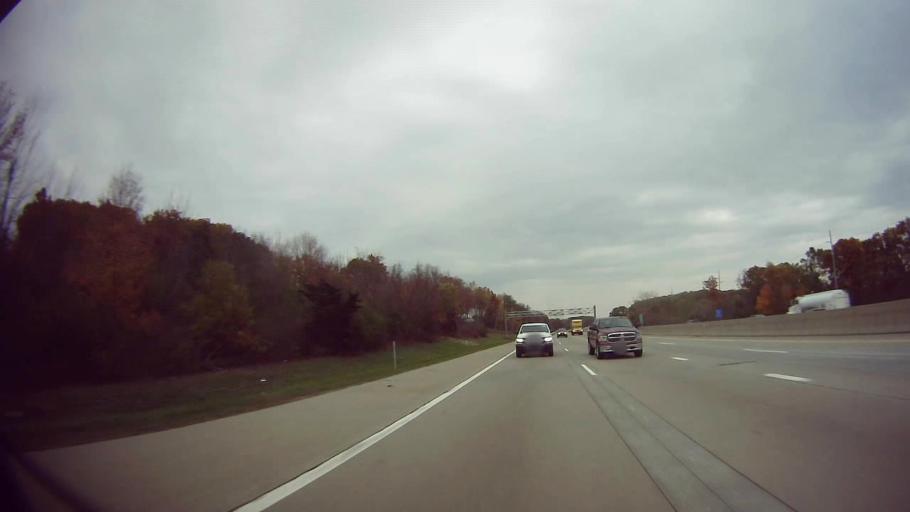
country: US
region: Michigan
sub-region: Oakland County
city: Farmington Hills
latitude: 42.4926
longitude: -83.4132
